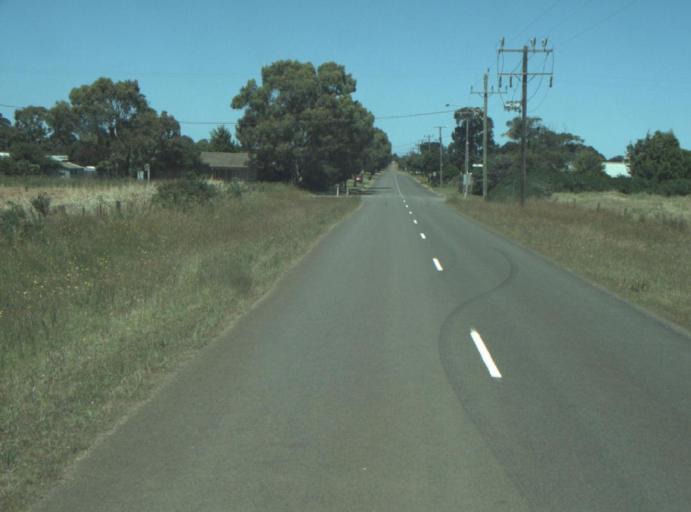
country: AU
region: Victoria
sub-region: Queenscliffe
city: Queenscliff
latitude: -38.1731
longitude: 144.7014
